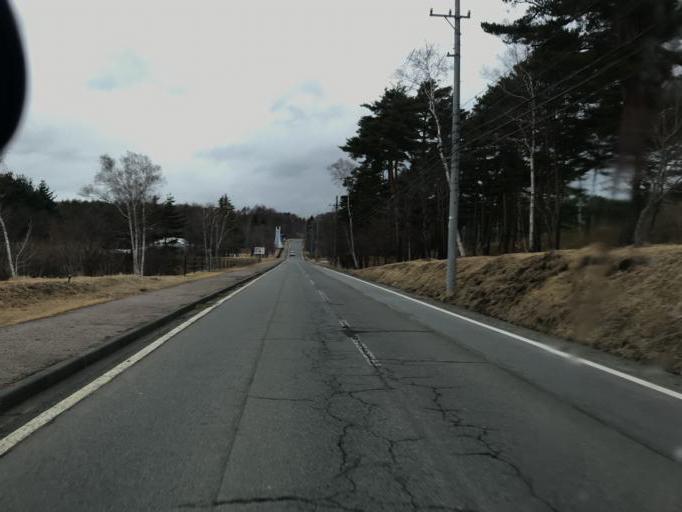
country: JP
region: Nagano
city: Chino
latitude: 35.9138
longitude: 138.3074
